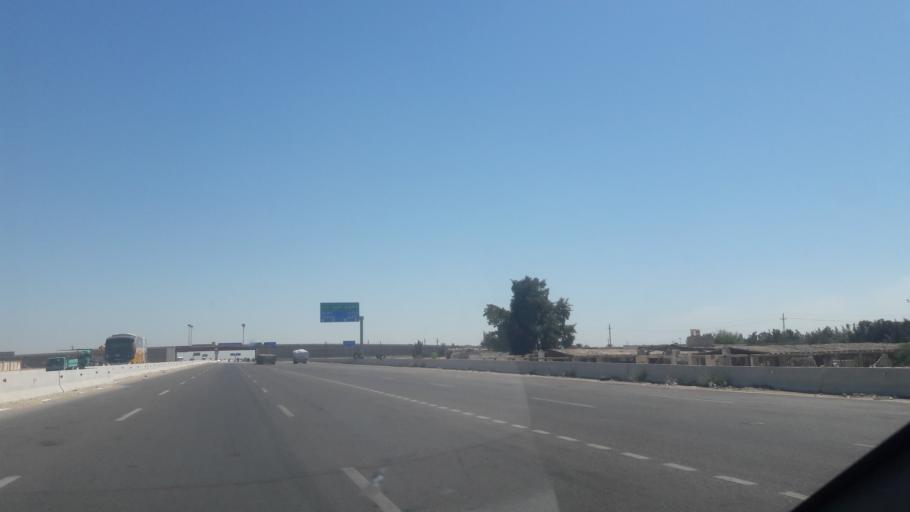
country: EG
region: Al Isma'iliyah
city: Ismailia
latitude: 30.8044
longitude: 32.1657
